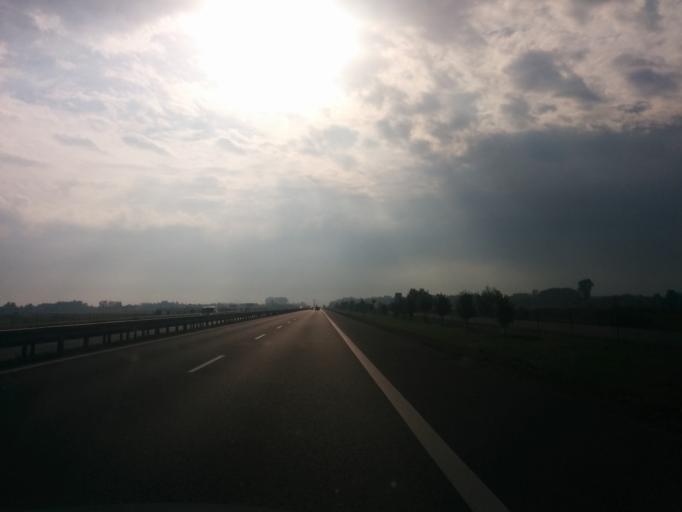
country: PL
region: Masovian Voivodeship
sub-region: Powiat radomski
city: Jedlinsk
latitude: 51.5377
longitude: 21.0693
